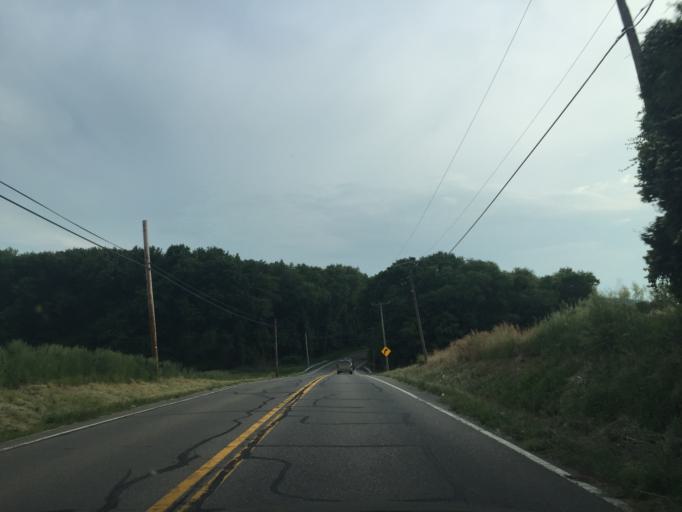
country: US
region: Maryland
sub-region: Frederick County
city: Brunswick
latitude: 39.3306
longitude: -77.6485
